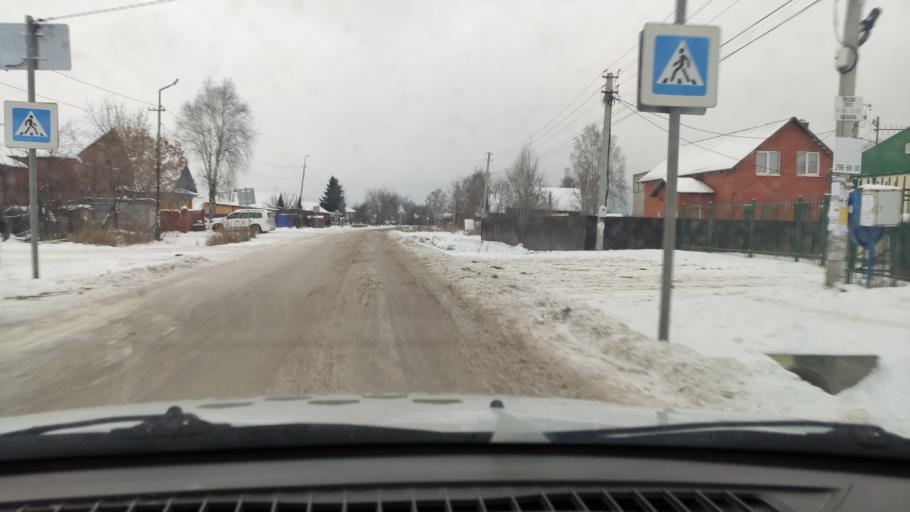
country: RU
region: Perm
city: Froly
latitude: 57.8862
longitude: 56.2575
